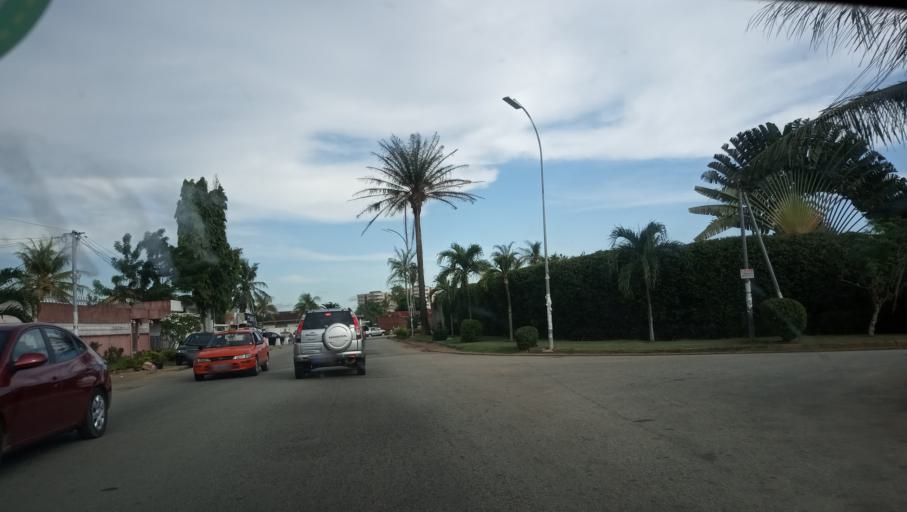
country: CI
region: Lagunes
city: Abidjan
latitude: 5.3487
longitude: -3.9806
